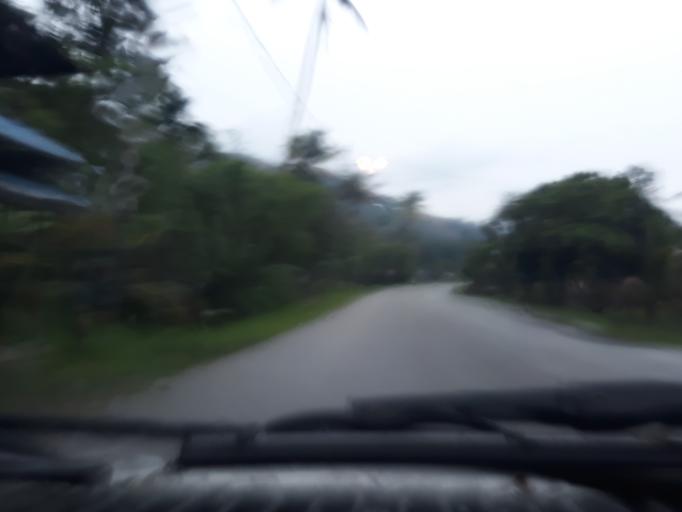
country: MY
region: Kedah
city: Kulim
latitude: 5.2705
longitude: 100.6140
